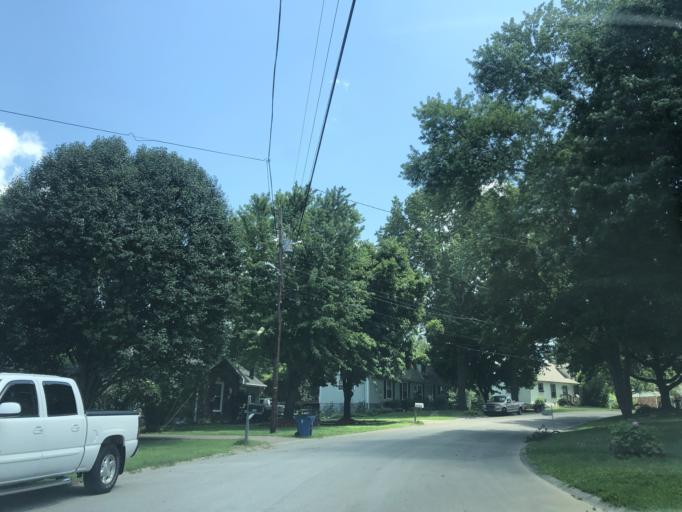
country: US
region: Tennessee
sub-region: Wilson County
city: Green Hill
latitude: 36.2192
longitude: -86.5856
